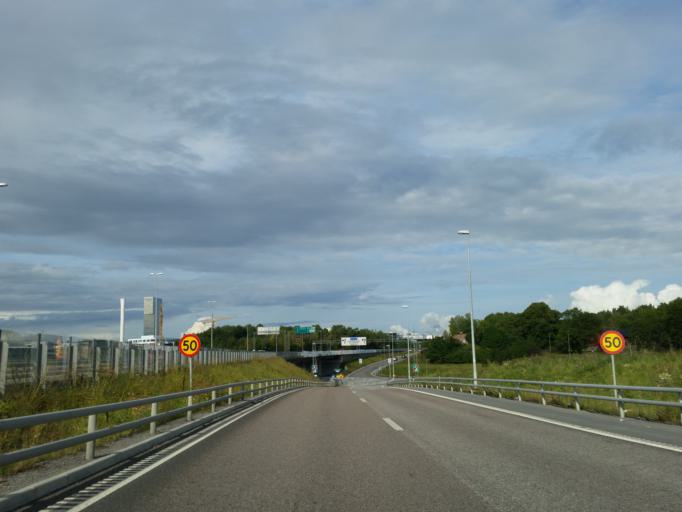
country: SE
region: Stockholm
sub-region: Stockholms Kommun
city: Kista
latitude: 59.3952
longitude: 17.9508
